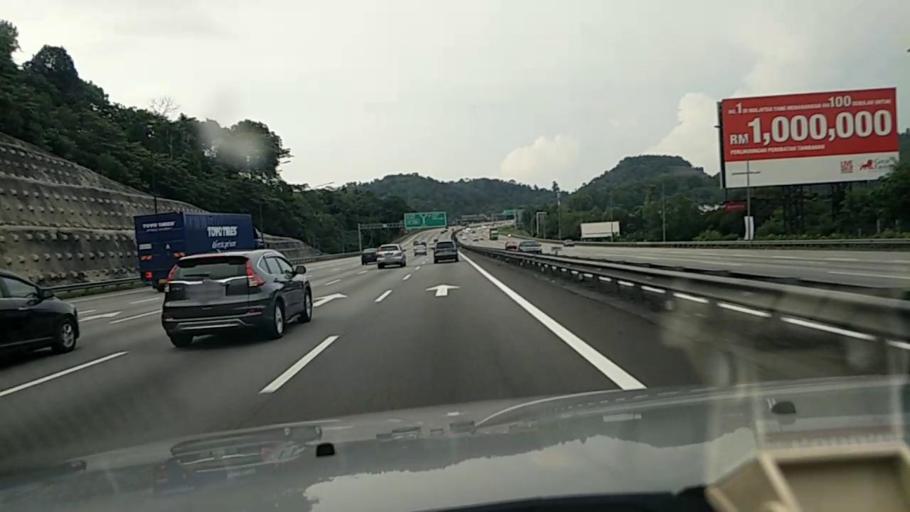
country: MY
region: Selangor
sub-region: Petaling
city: Petaling Jaya
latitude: 3.1616
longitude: 101.5976
